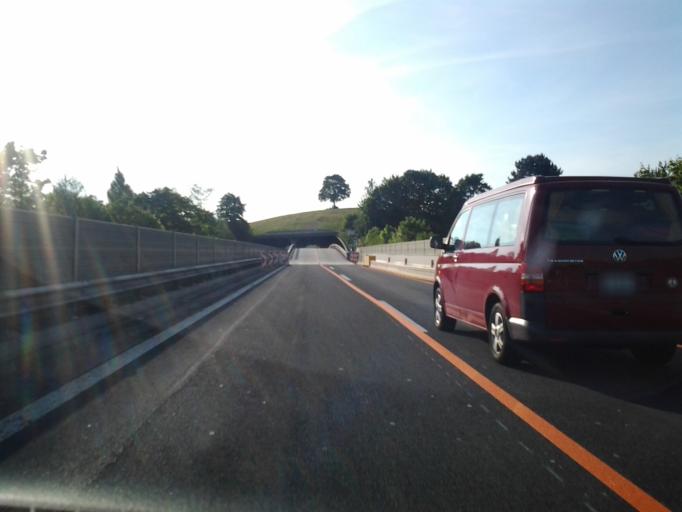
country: CH
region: Lucerne
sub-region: Sursee District
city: Schenkon
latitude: 47.1743
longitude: 8.1280
